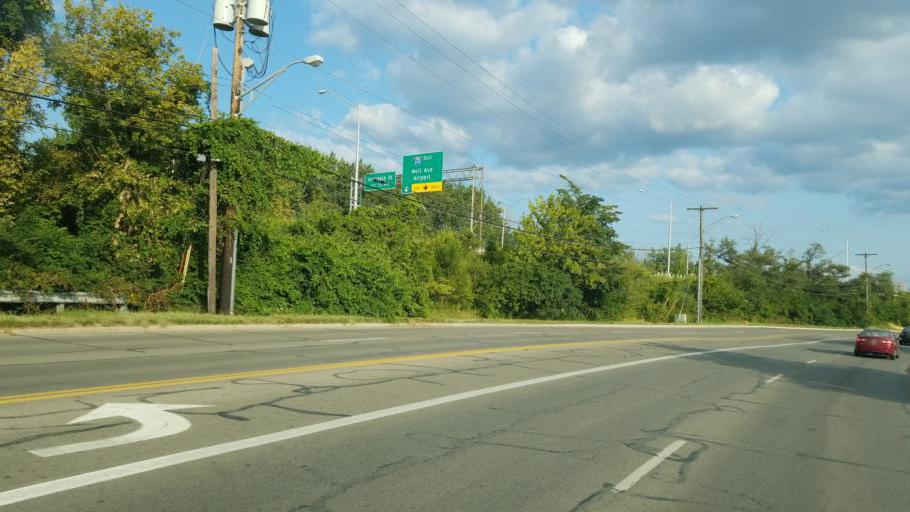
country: US
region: Ohio
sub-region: Franklin County
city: Grandview Heights
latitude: 39.9858
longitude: -83.0235
